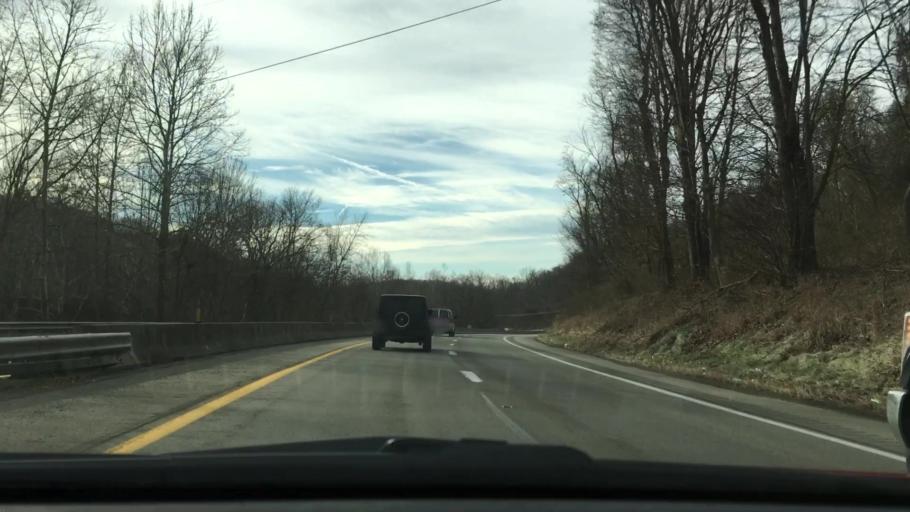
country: US
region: Pennsylvania
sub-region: Fayette County
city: Perryopolis
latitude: 39.9998
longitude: -79.7620
